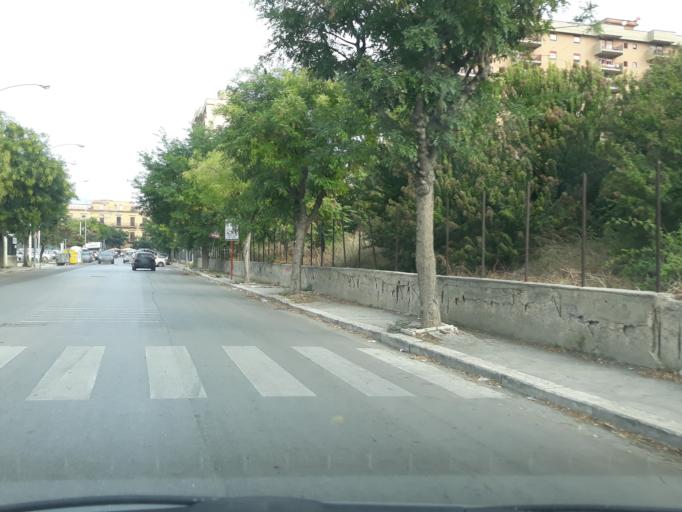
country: IT
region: Sicily
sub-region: Palermo
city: Palermo
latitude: 38.0988
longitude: 13.3255
